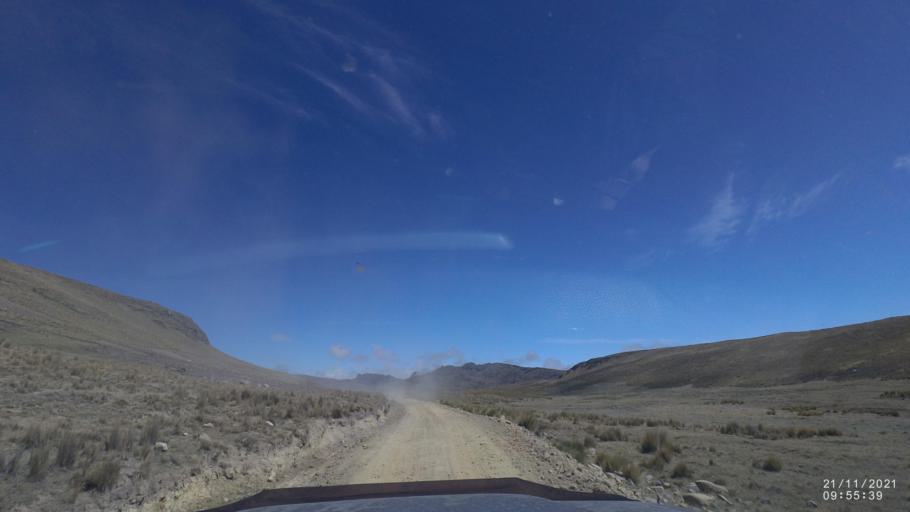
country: BO
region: Cochabamba
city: Cochabamba
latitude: -17.0459
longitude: -66.2636
